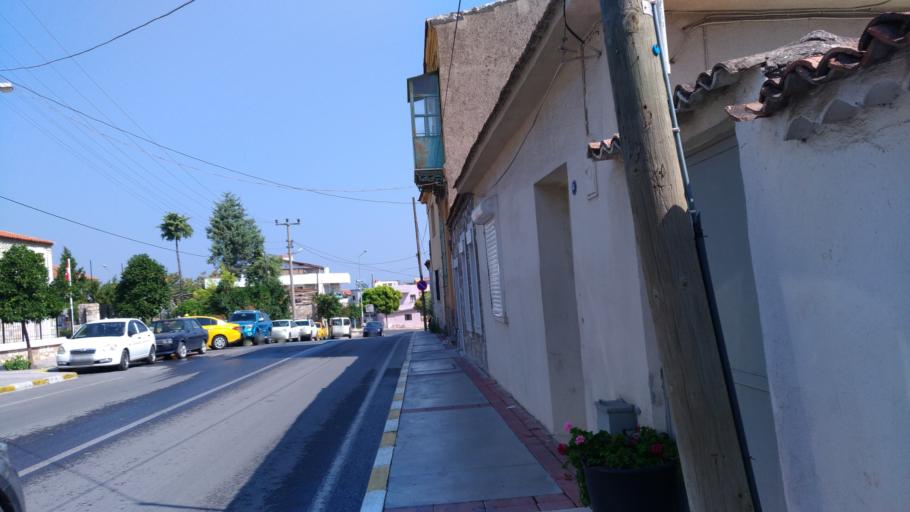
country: TR
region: Izmir
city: Urla
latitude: 38.3226
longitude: 26.7641
